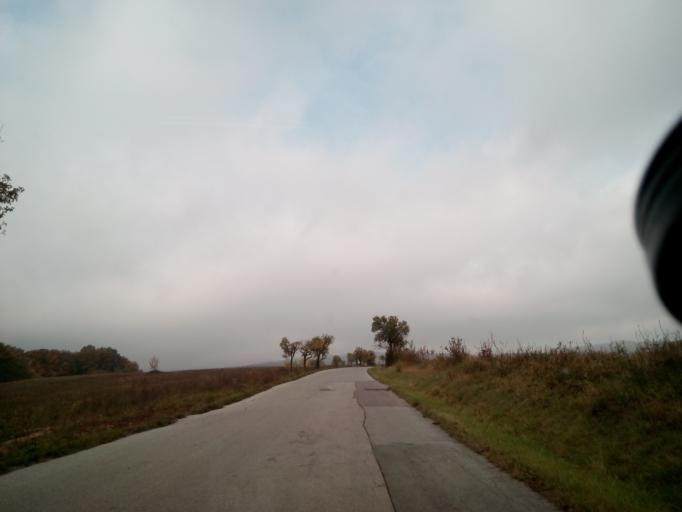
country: SK
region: Kosicky
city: Kosice
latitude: 48.7333
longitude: 21.1304
